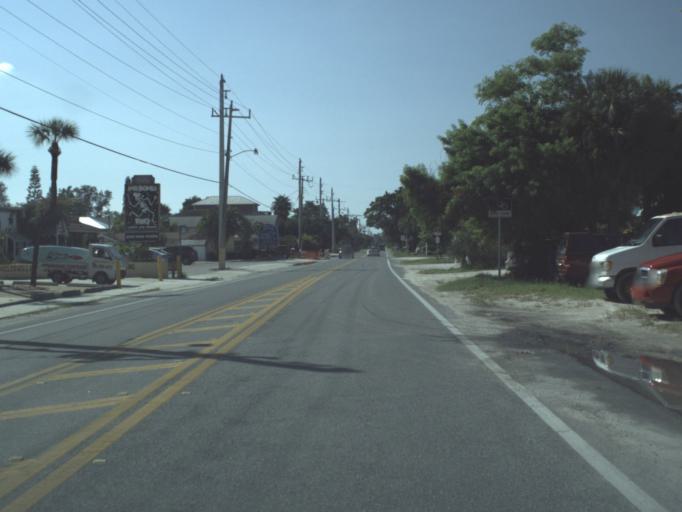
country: US
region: Florida
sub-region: Manatee County
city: Holmes Beach
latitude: 27.4905
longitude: -82.7071
